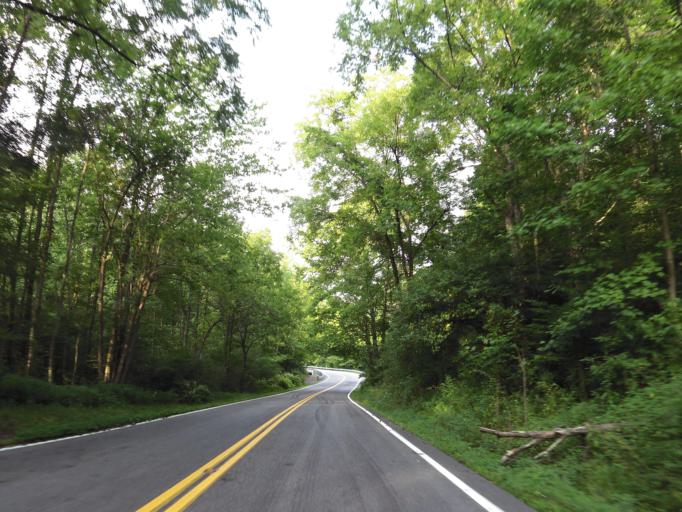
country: US
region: Tennessee
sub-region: Morgan County
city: Coalfield
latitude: 36.1244
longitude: -84.4243
